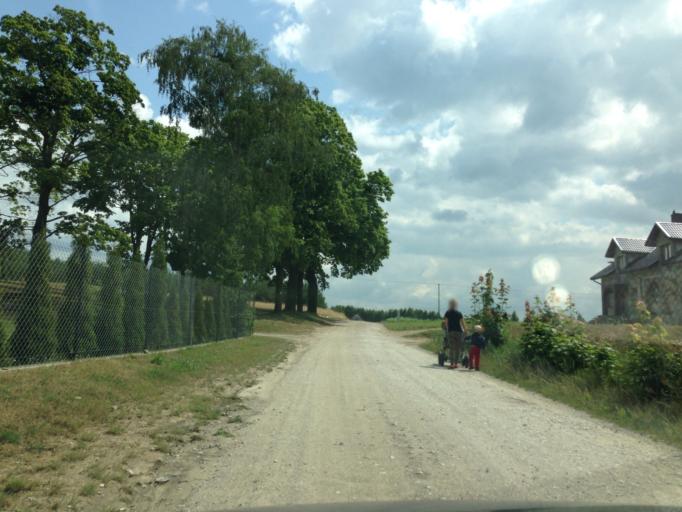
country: PL
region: Kujawsko-Pomorskie
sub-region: Powiat brodnicki
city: Gorzno
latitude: 53.2276
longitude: 19.6388
